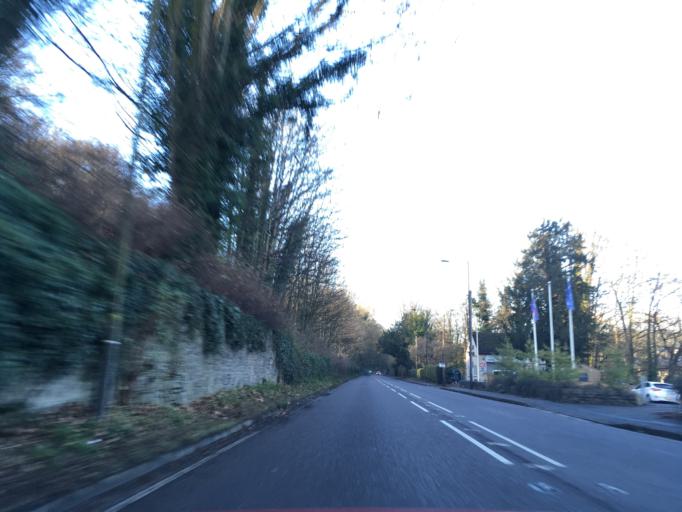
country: GB
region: England
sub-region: Bath and North East Somerset
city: Bath
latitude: 51.3821
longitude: -2.3986
